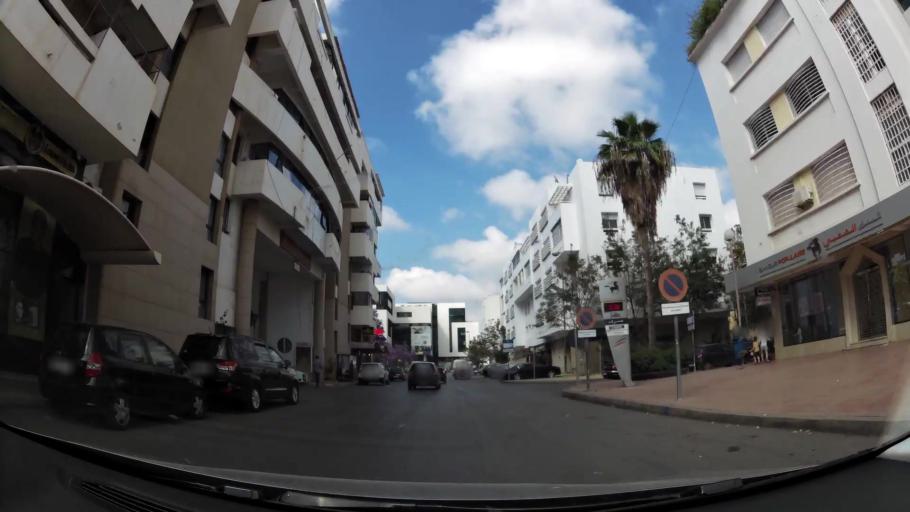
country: MA
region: Rabat-Sale-Zemmour-Zaer
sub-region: Skhirate-Temara
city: Temara
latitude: 33.9607
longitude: -6.8666
